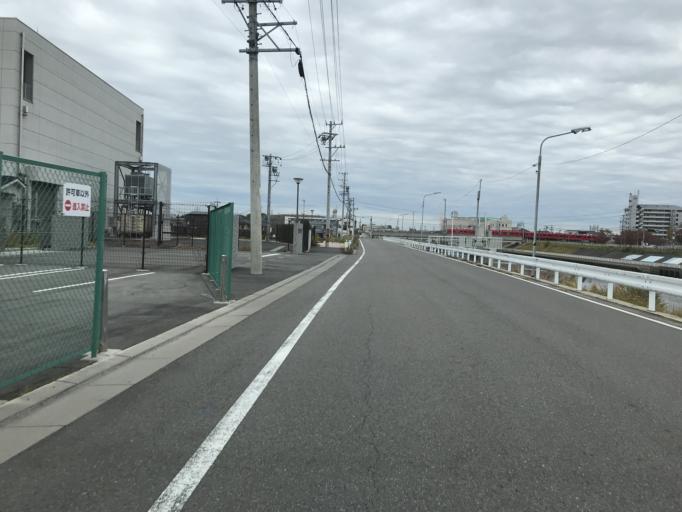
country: JP
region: Aichi
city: Nagoya-shi
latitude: 35.1980
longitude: 136.8533
